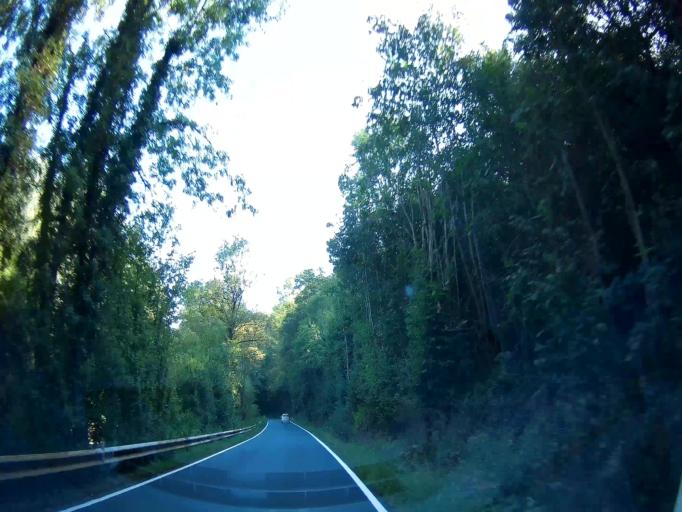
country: BE
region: Wallonia
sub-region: Province de Namur
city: Mettet
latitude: 50.3122
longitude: 4.7613
